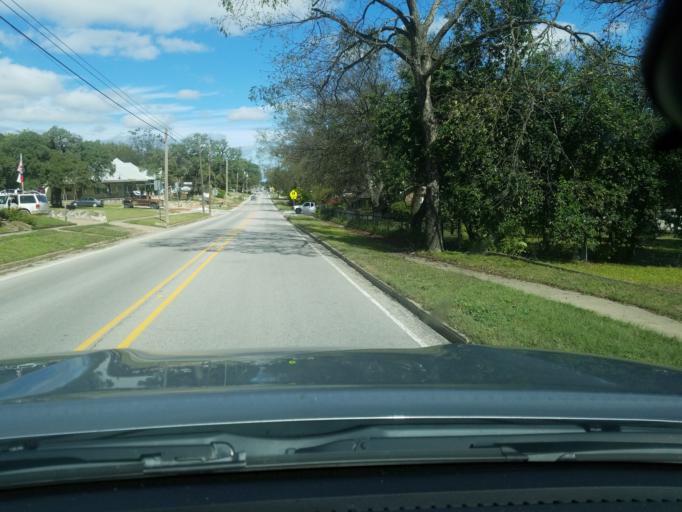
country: US
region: Texas
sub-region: Hamilton County
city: Hamilton
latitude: 31.6994
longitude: -98.1258
